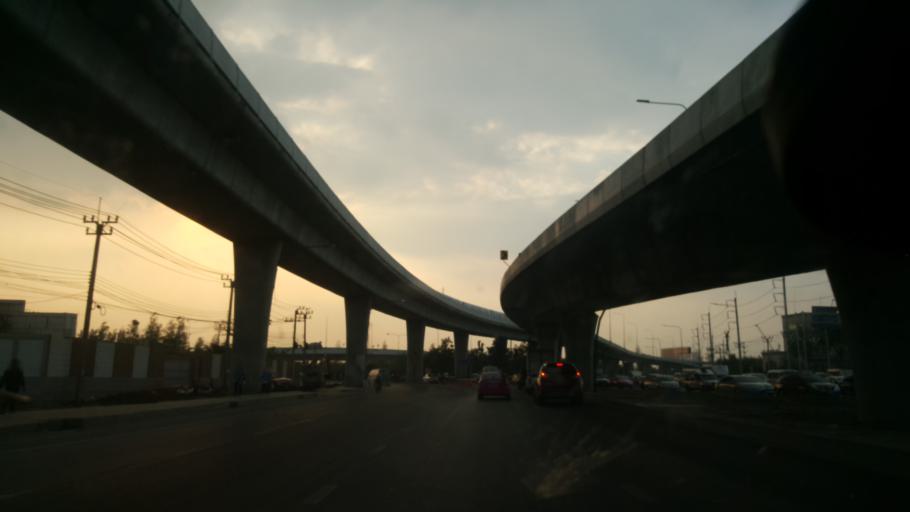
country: TH
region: Bangkok
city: Bangkok Yai
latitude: 13.7143
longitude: 100.4646
